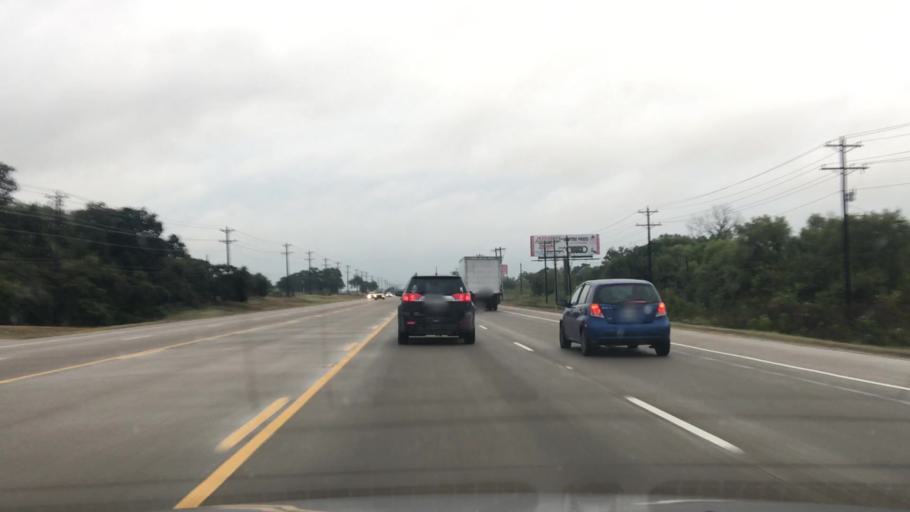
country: US
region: Texas
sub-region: Denton County
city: Oak Point
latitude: 33.2216
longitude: -96.9504
